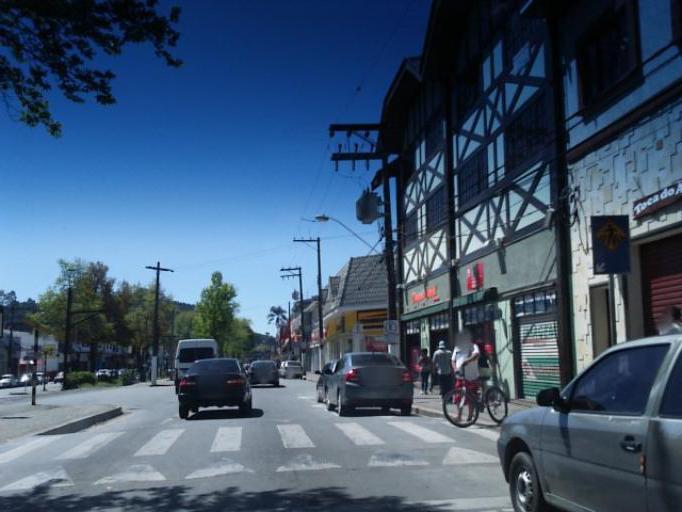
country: BR
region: Sao Paulo
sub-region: Campos Do Jordao
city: Campos do Jordao
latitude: -22.7411
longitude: -45.5945
